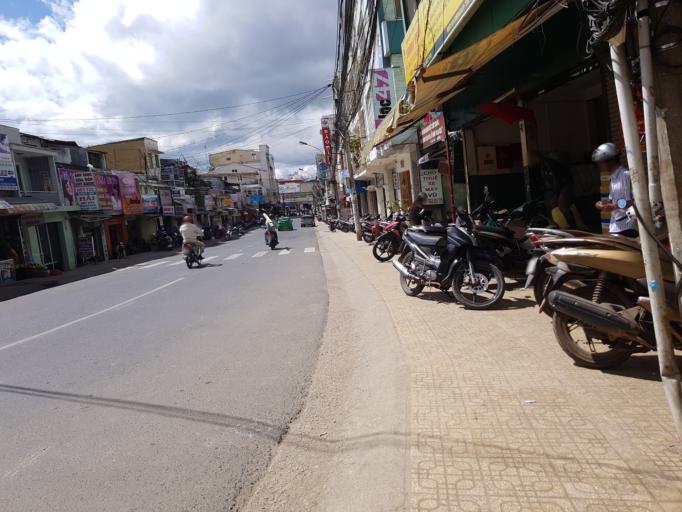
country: VN
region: Lam Dong
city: Da Lat
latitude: 11.9444
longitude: 108.4377
